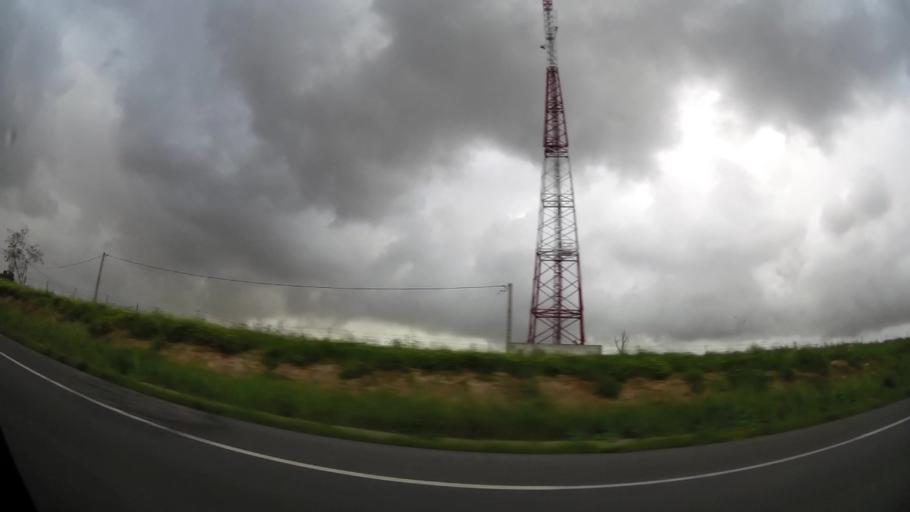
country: MA
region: Grand Casablanca
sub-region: Mediouna
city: Tit Mellil
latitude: 33.5925
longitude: -7.4481
